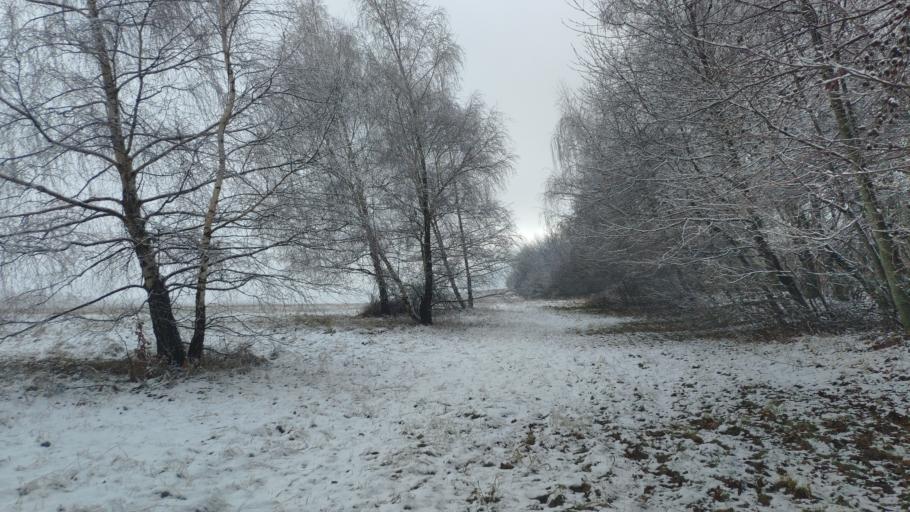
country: SK
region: Kosicky
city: Moldava nad Bodvou
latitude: 48.7400
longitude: 21.0873
